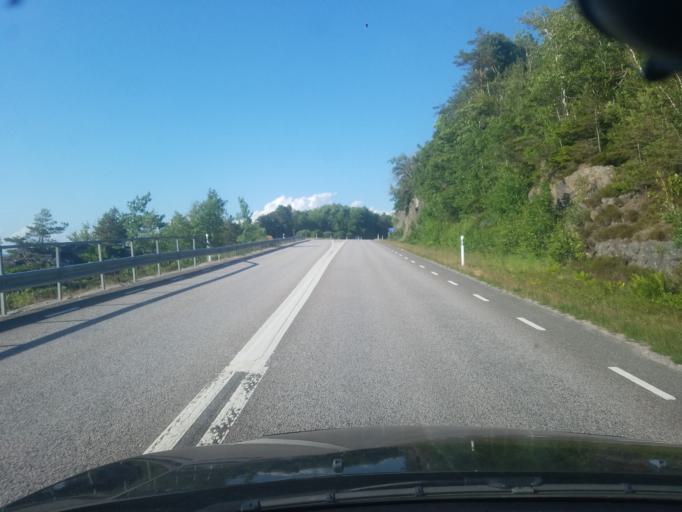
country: SE
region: Vaestra Goetaland
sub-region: Orust
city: Henan
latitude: 58.2612
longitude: 11.6791
